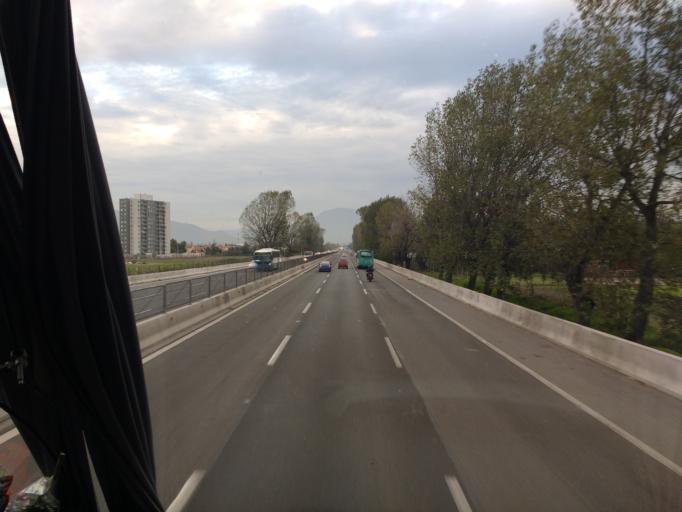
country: CL
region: Santiago Metropolitan
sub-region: Provincia de Santiago
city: Lo Prado
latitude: -33.4503
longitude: -70.7556
